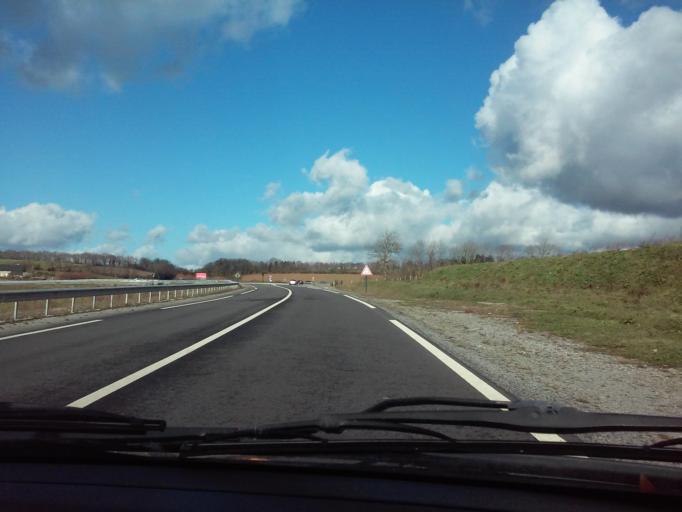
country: FR
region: Brittany
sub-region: Departement d'Ille-et-Vilaine
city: Vitre
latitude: 48.0937
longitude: -1.2265
